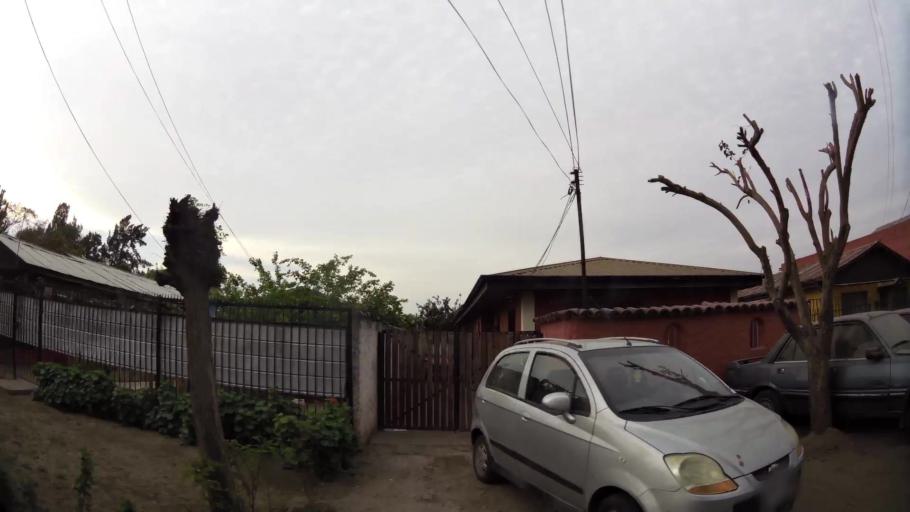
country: CL
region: Santiago Metropolitan
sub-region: Provincia de Santiago
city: Lo Prado
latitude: -33.5147
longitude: -70.7761
